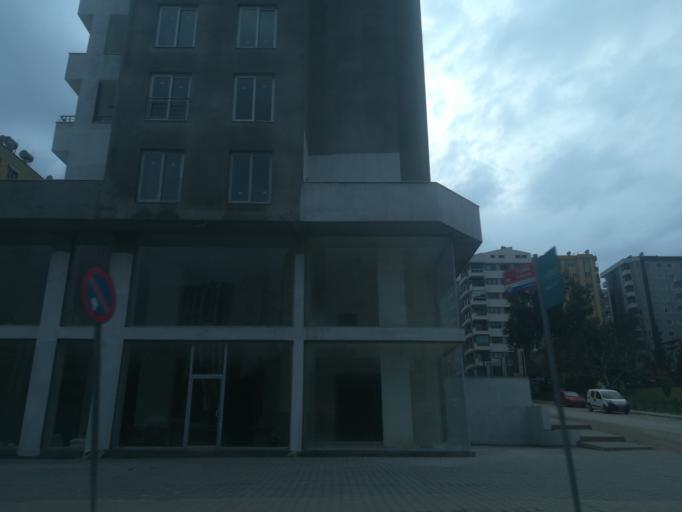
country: TR
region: Adana
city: Adana
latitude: 37.0392
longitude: 35.2930
